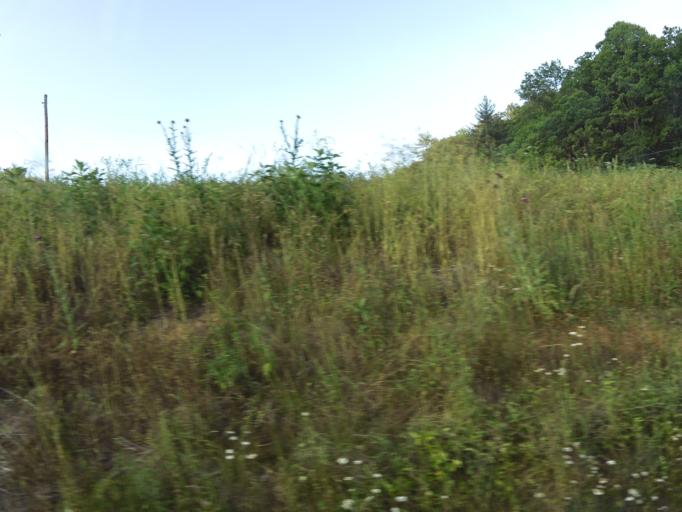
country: US
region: Tennessee
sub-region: Sevier County
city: Sevierville
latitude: 35.8304
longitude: -83.6125
